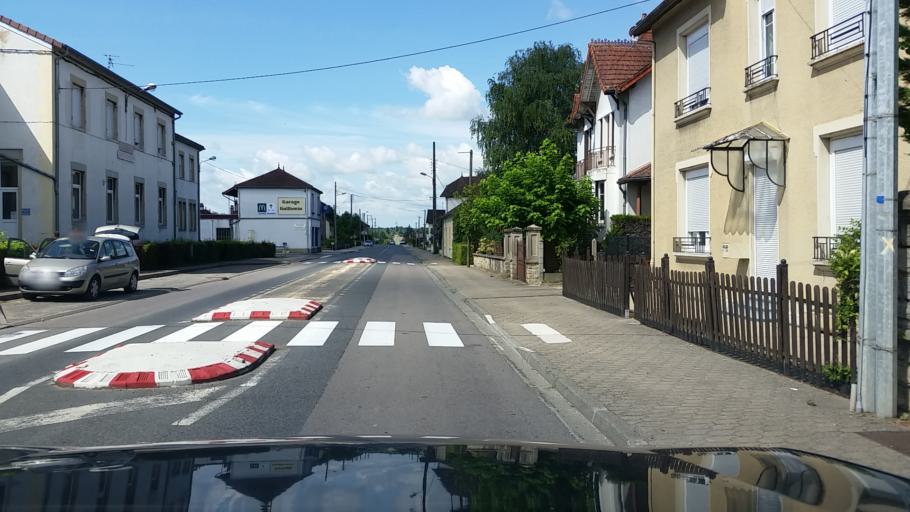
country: FR
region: Bourgogne
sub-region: Departement de Saone-et-Loire
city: Saint-Germain-du-Bois
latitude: 46.7531
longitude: 5.2394
